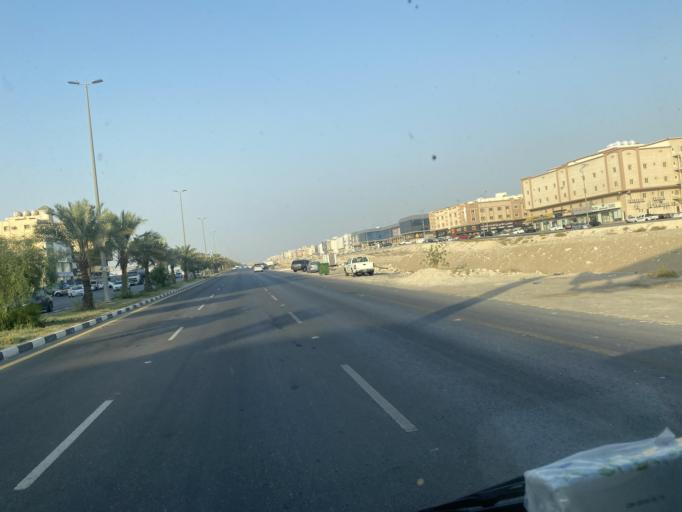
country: SA
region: Eastern Province
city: Dammam
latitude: 26.3625
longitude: 50.0703
